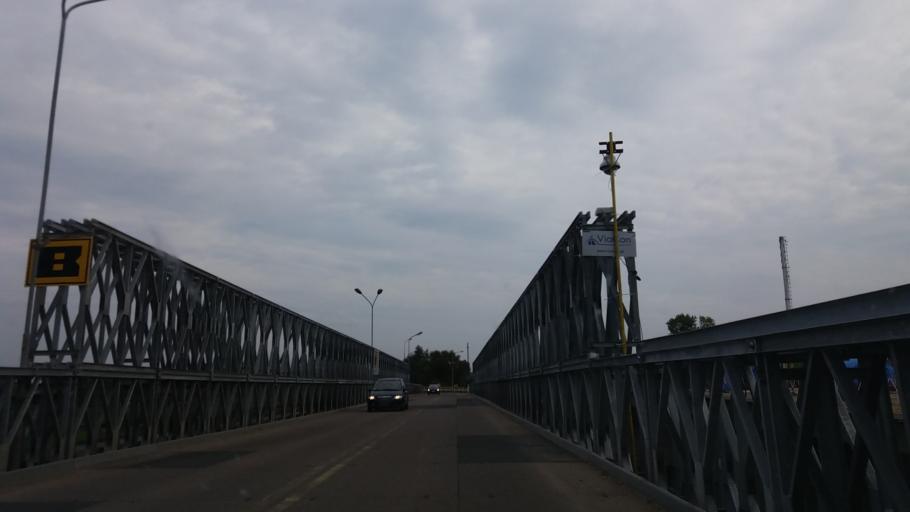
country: PL
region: Lubusz
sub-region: Powiat miedzyrzecki
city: Skwierzyna
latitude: 52.6027
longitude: 15.5000
